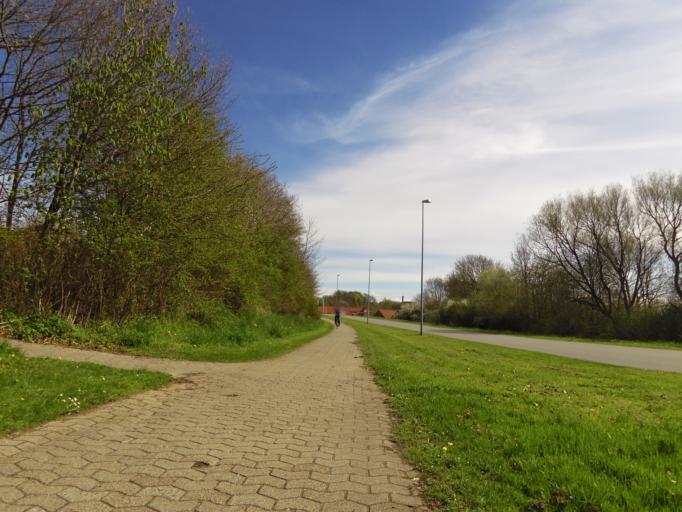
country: DK
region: Central Jutland
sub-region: Skive Kommune
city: Skive
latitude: 56.5866
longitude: 9.0247
